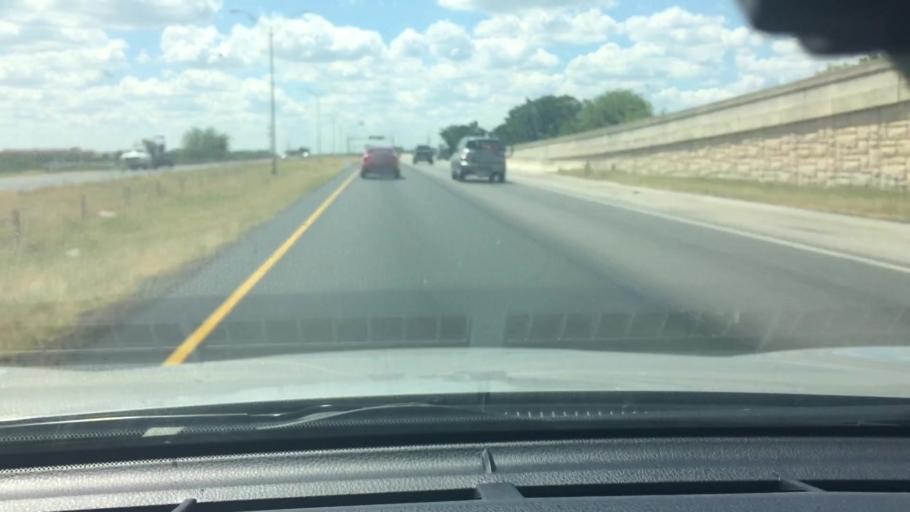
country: US
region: Texas
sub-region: Bexar County
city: Shavano Park
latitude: 29.5894
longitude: -98.6165
